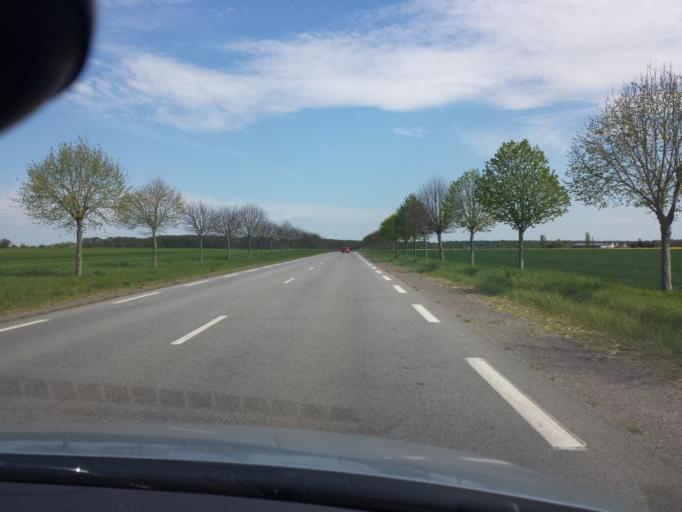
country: FR
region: Haute-Normandie
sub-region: Departement de l'Eure
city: Breteuil
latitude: 48.8444
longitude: 0.9258
